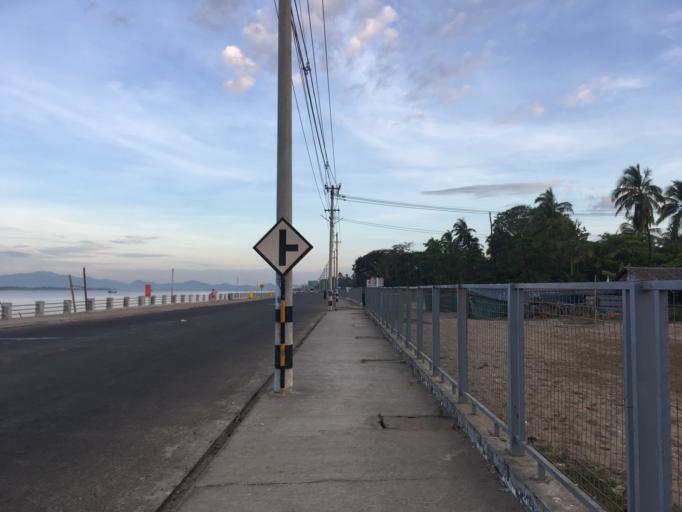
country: MM
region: Mon
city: Mawlamyine
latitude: 16.4581
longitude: 97.6235
